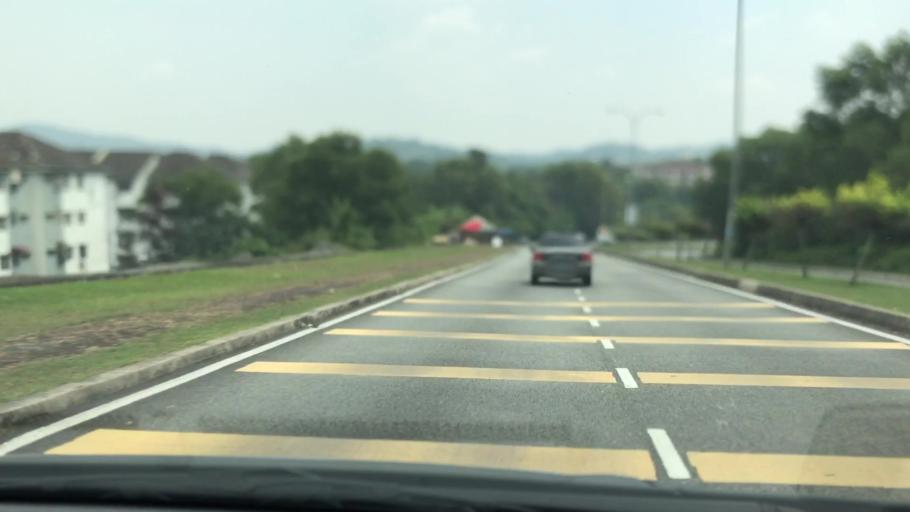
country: MY
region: Putrajaya
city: Putrajaya
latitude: 2.9908
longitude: 101.6635
